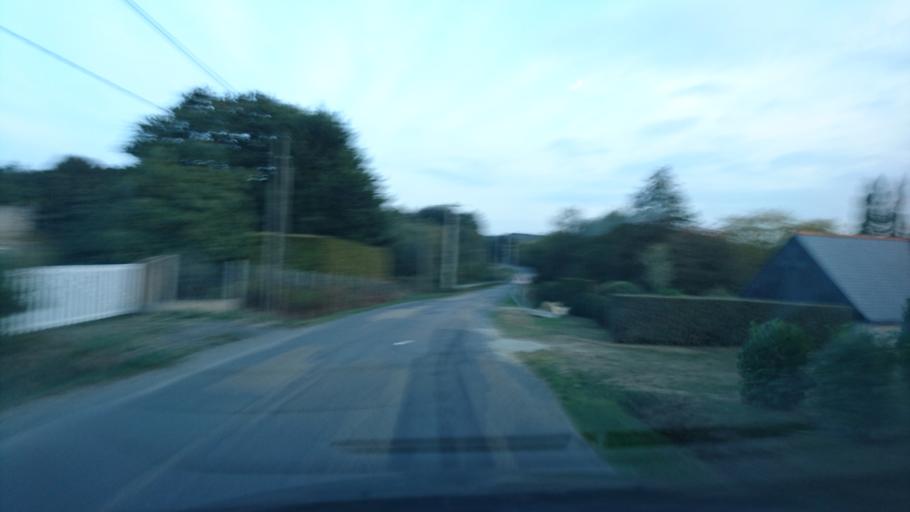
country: FR
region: Brittany
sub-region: Departement d'Ille-et-Vilaine
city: Maure-de-Bretagne
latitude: 47.9022
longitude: -1.9499
